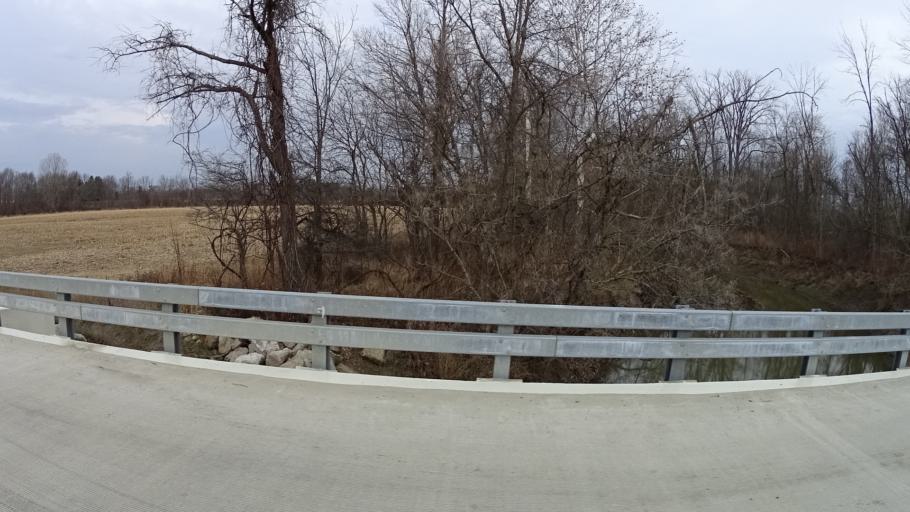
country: US
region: Ohio
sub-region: Lorain County
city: Lagrange
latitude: 41.1542
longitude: -82.1195
